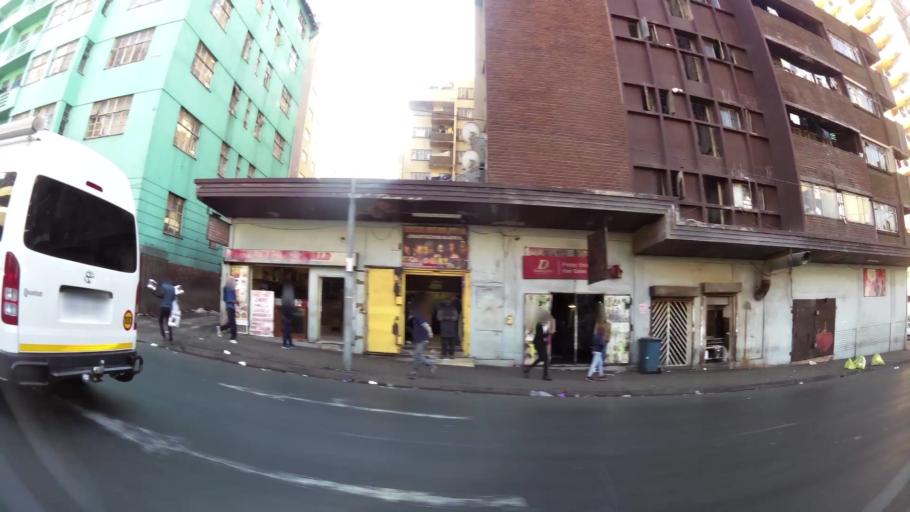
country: ZA
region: Gauteng
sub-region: City of Johannesburg Metropolitan Municipality
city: Johannesburg
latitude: -26.1910
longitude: 28.0475
